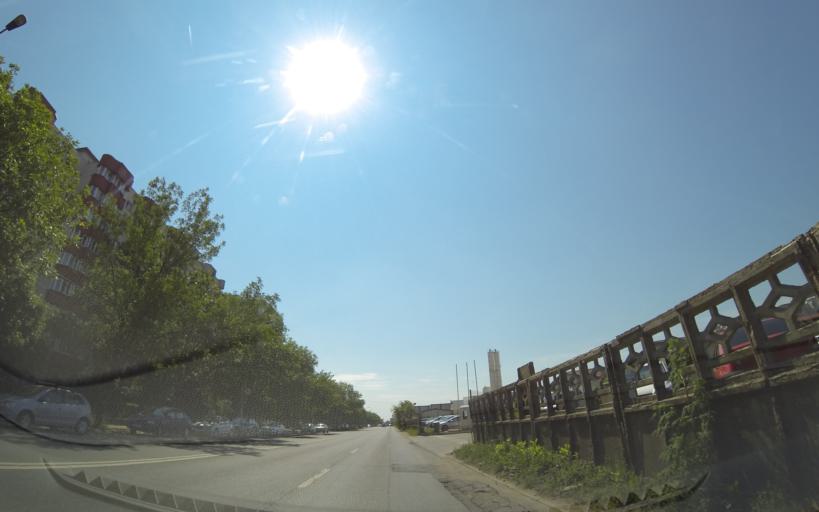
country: RO
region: Bucuresti
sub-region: Municipiul Bucuresti
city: Bucuresti
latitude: 44.4250
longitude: 26.0663
